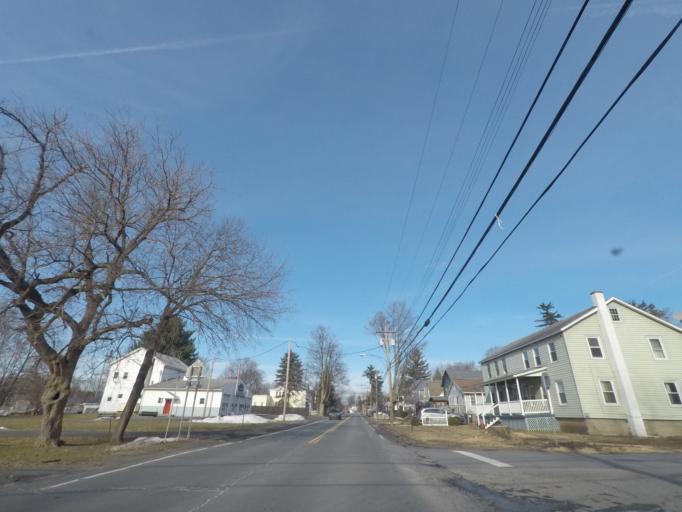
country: US
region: New York
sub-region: Rensselaer County
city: Nassau
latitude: 42.5134
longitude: -73.6109
